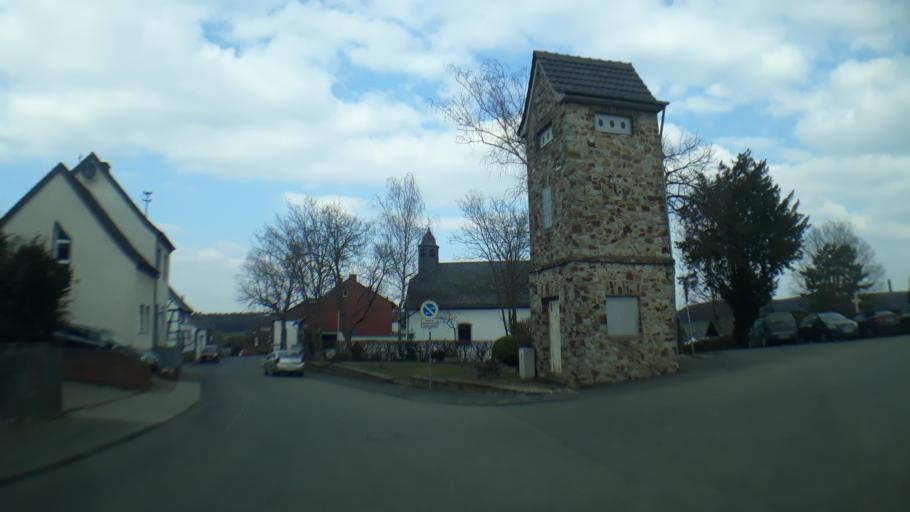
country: DE
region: North Rhine-Westphalia
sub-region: Regierungsbezirk Koln
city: Rheinbach
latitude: 50.5937
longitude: 6.8914
